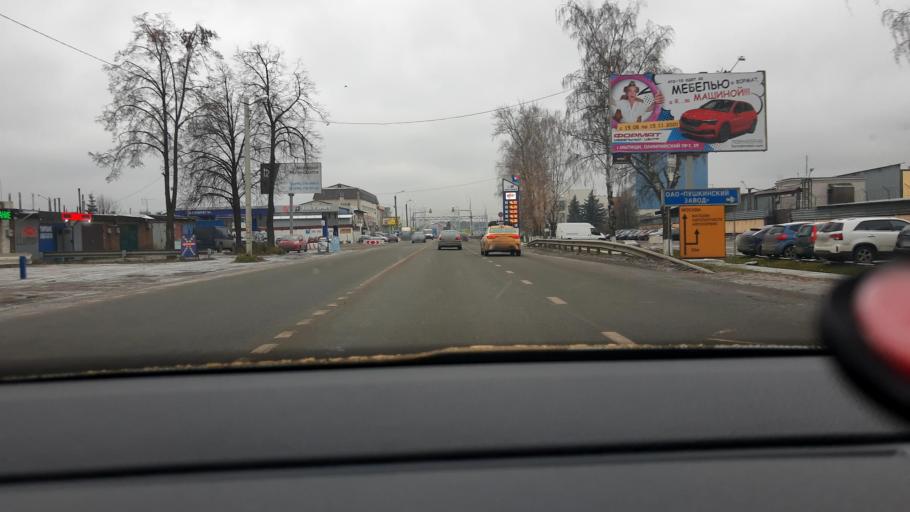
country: RU
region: Moskovskaya
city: Lesnyye Polyany
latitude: 55.9841
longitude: 37.8656
